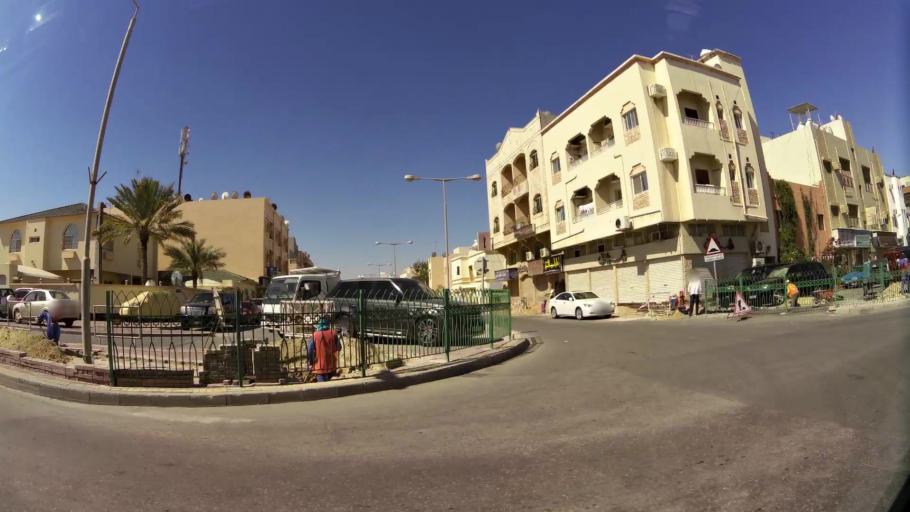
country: BH
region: Muharraq
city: Al Muharraq
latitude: 26.2554
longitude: 50.6196
